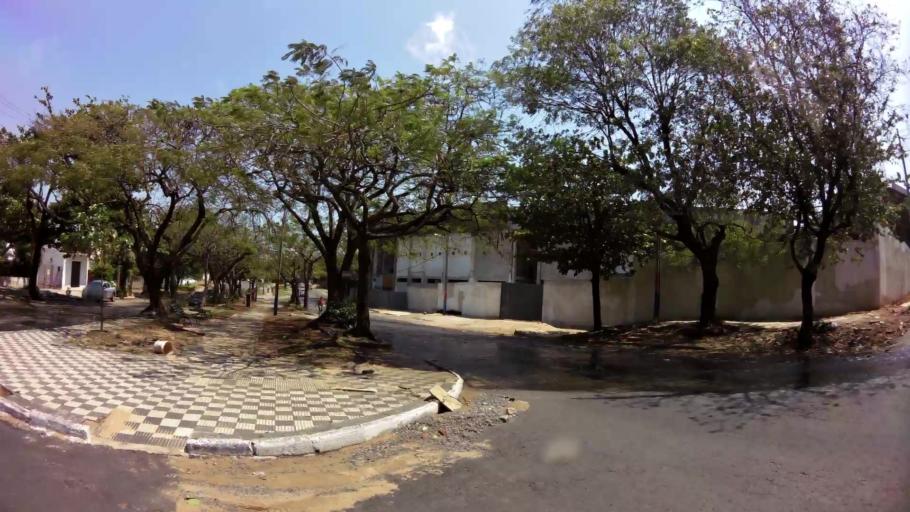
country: PY
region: Asuncion
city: Asuncion
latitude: -25.3011
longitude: -57.6374
